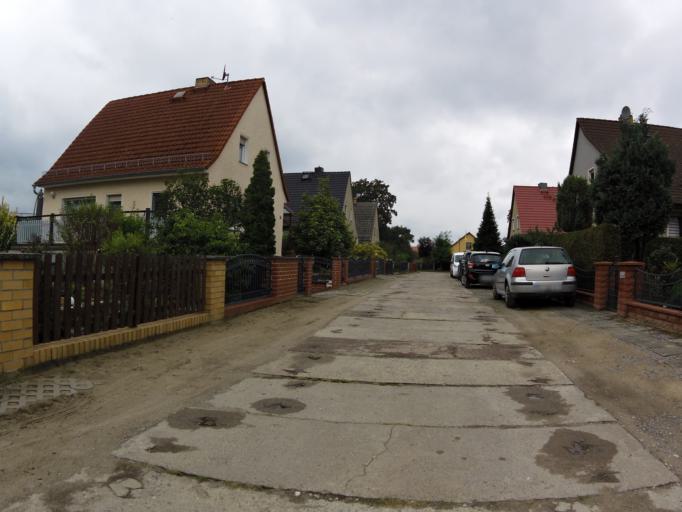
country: DE
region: Brandenburg
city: Storkow
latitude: 52.2636
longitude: 13.9437
